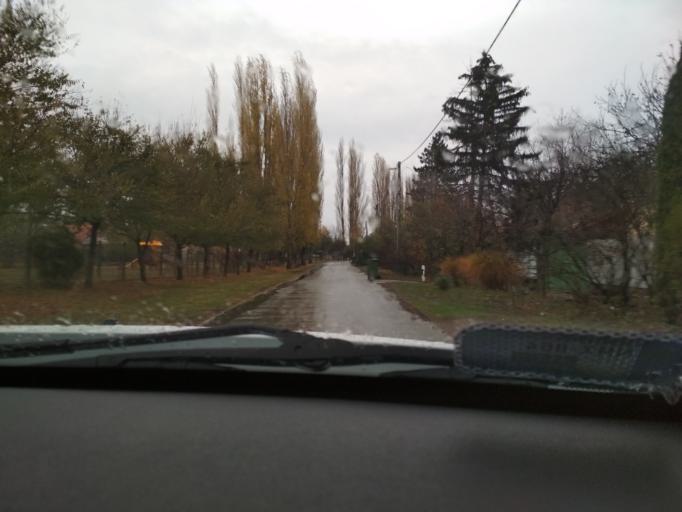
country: HU
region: Csongrad
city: Opusztaszer
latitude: 46.4360
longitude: 20.1365
